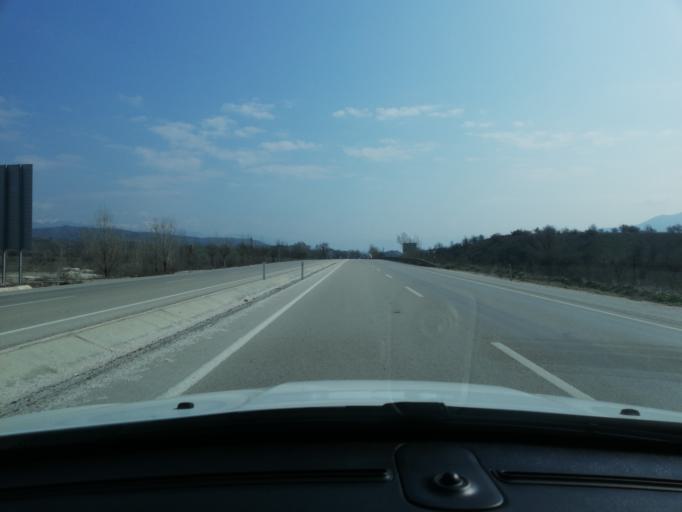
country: TR
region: Cankiri
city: Beloren
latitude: 40.8708
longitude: 33.4943
